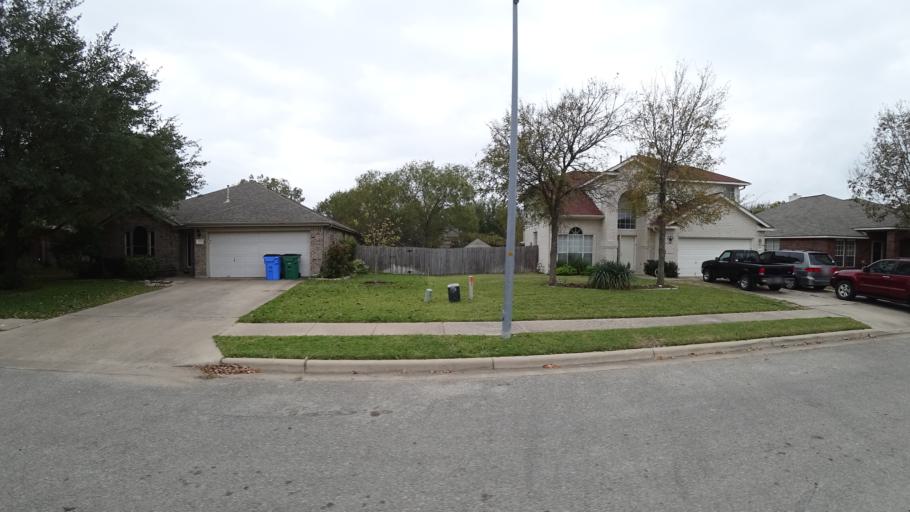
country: US
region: Texas
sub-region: Travis County
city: Pflugerville
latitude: 30.4377
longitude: -97.6070
